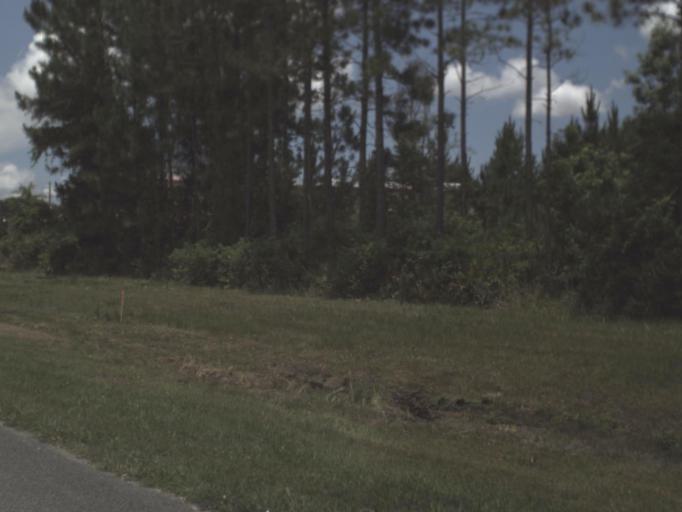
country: US
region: Florida
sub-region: Nassau County
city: Yulee
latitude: 30.6277
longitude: -81.5999
